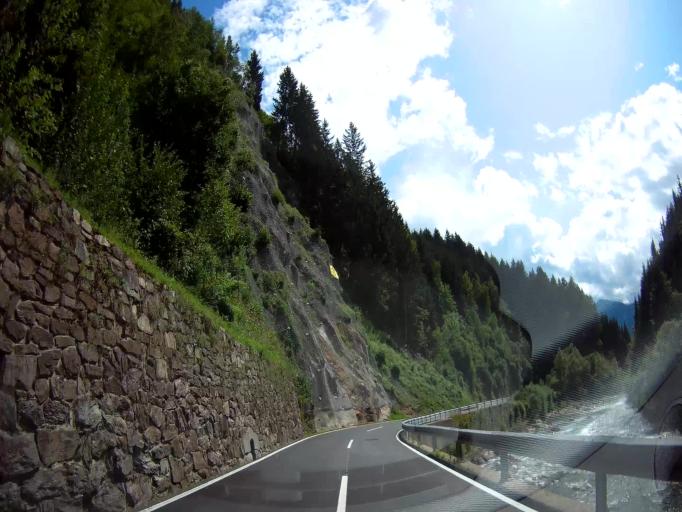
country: AT
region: Carinthia
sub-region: Politischer Bezirk Spittal an der Drau
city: Seeboden
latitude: 46.8487
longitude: 13.5035
